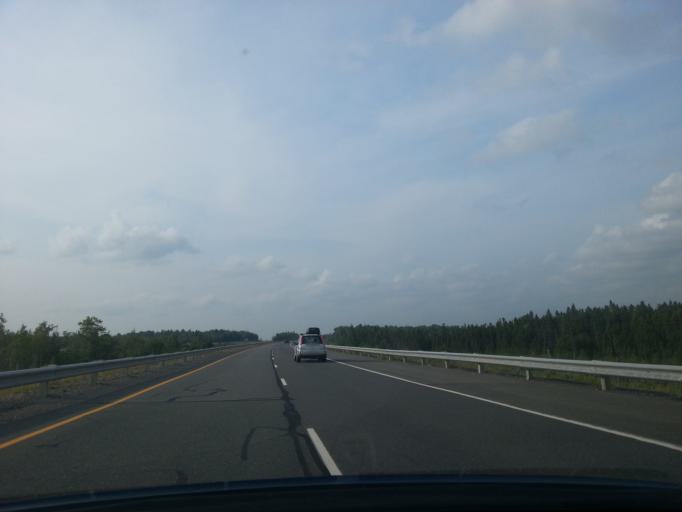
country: CA
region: New Brunswick
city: Florenceville-Bristol
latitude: 46.3525
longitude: -67.6128
